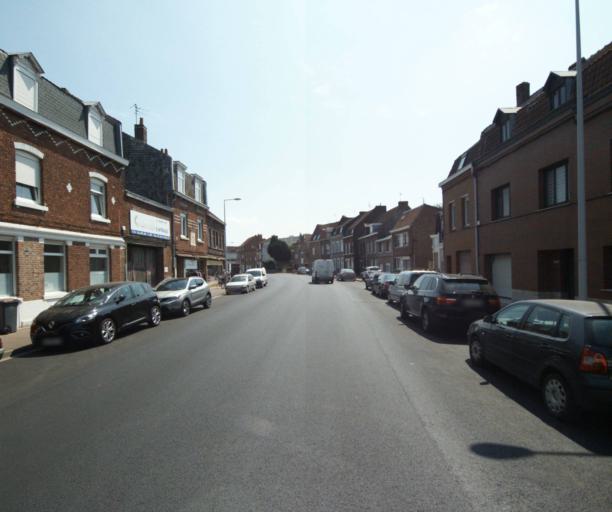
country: FR
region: Nord-Pas-de-Calais
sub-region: Departement du Nord
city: Saint-Andre-lez-Lille
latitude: 50.6713
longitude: 3.0517
